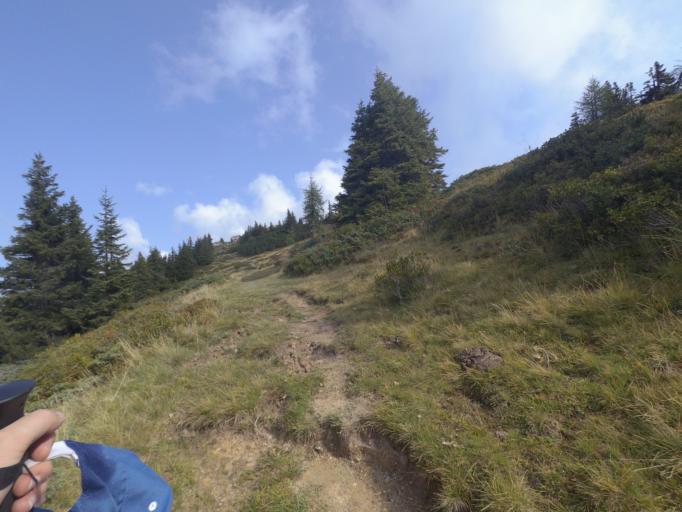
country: AT
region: Salzburg
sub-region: Politischer Bezirk Sankt Johann im Pongau
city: Kleinarl
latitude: 47.2648
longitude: 13.2775
